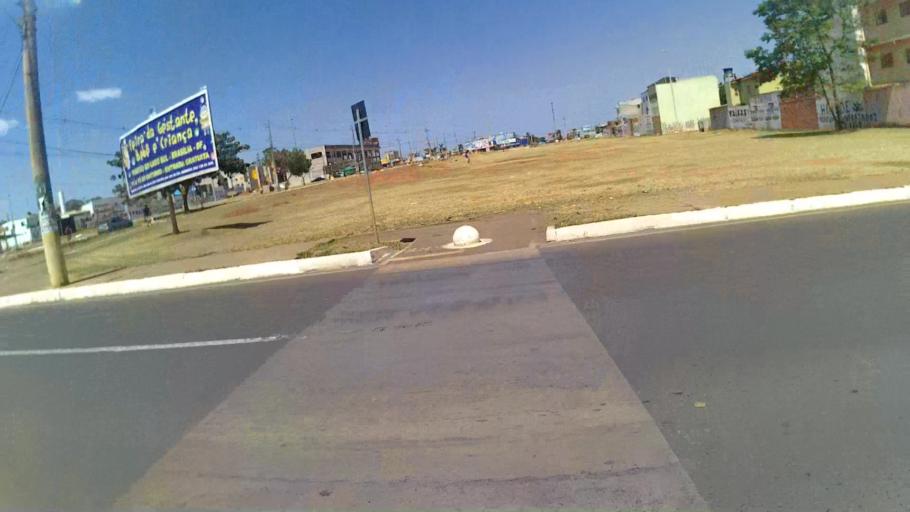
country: BR
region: Federal District
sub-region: Brasilia
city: Brasilia
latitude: -15.8988
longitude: -48.0482
